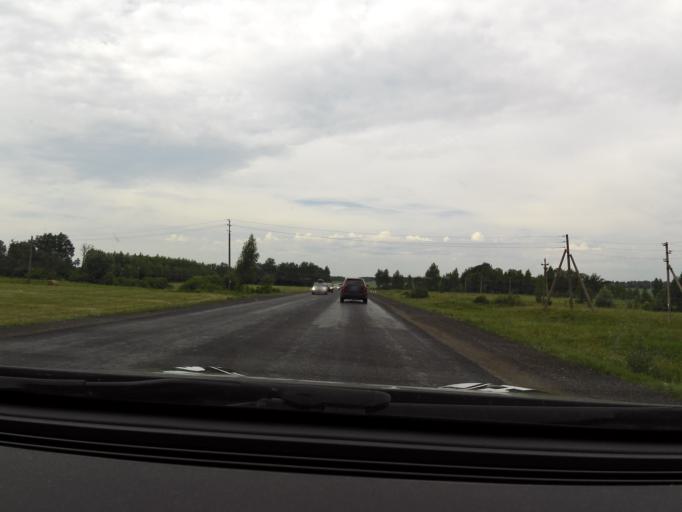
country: RU
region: Bashkortostan
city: Iglino
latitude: 54.7501
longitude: 56.3310
